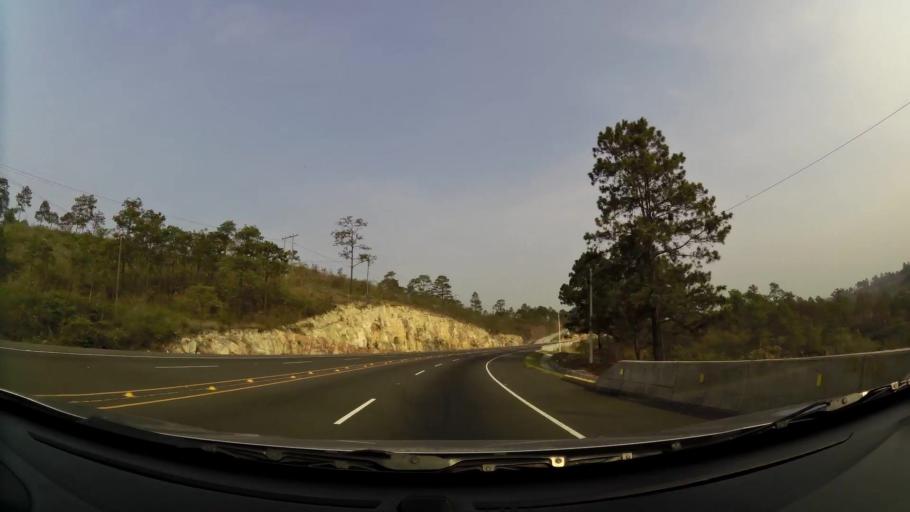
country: HN
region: Francisco Morazan
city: Zambrano
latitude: 14.2525
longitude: -87.3835
